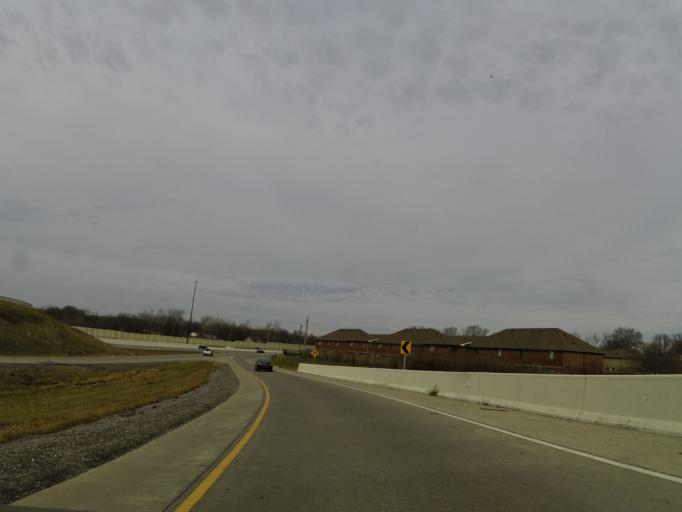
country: US
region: Indiana
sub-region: Marion County
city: Speedway
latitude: 39.8062
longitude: -86.2733
